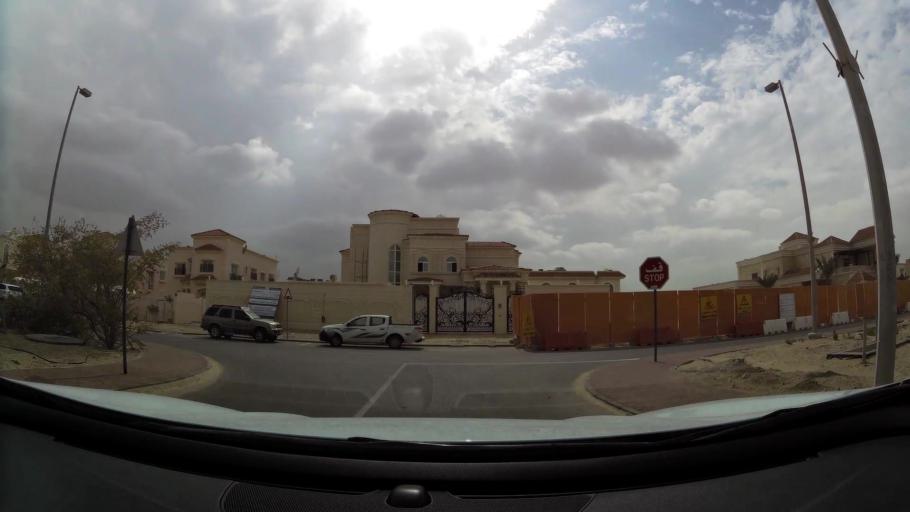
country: AE
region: Abu Dhabi
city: Abu Dhabi
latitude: 24.3827
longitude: 54.6403
